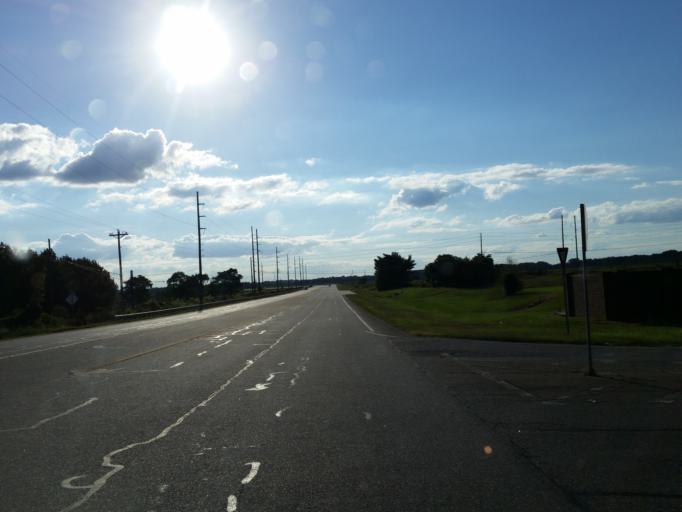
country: US
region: Georgia
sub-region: Houston County
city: Perry
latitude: 32.4901
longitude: -83.7518
